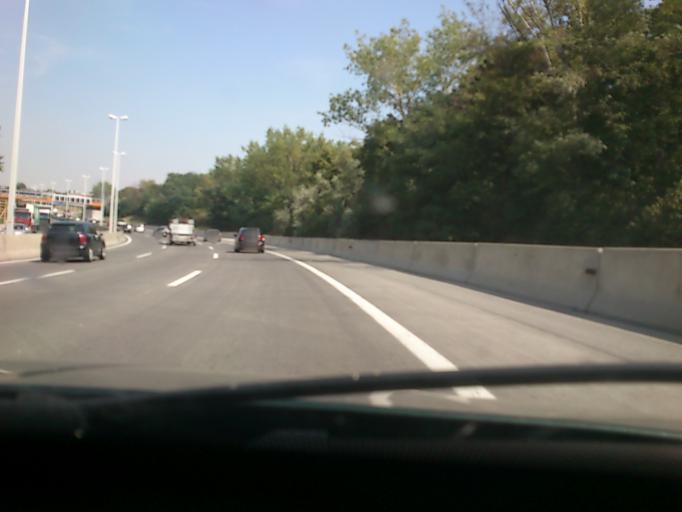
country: AT
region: Lower Austria
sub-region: Politischer Bezirk Wien-Umgebung
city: Leopoldsdorf
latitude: 48.1519
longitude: 16.3747
